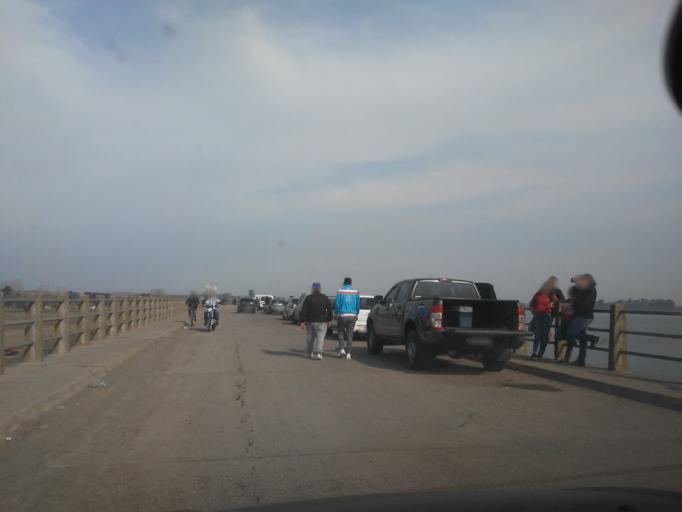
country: AR
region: Buenos Aires
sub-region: Partido de Marcos Paz
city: Marcos Paz
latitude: -34.6850
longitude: -58.8581
